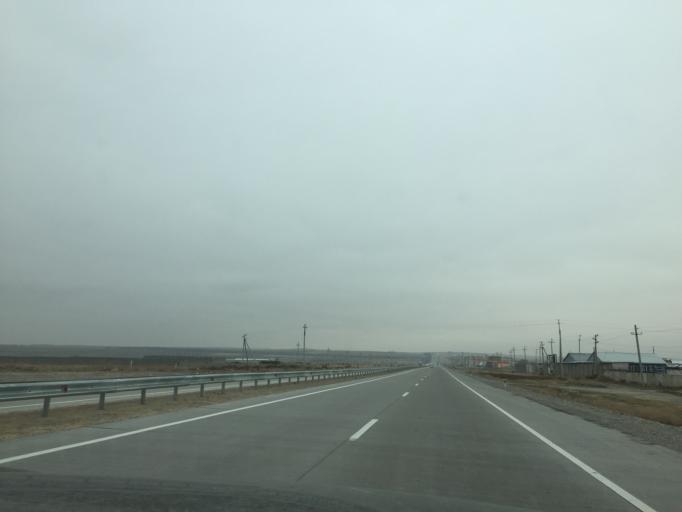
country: KZ
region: Ongtustik Qazaqstan
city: Aksu
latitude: 42.4747
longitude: 69.8217
